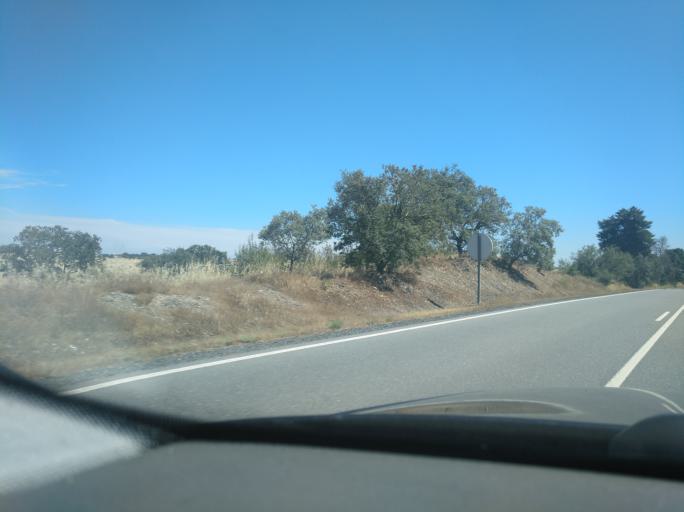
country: PT
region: Beja
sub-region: Castro Verde
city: Castro Verde
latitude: 37.6434
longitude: -8.0816
